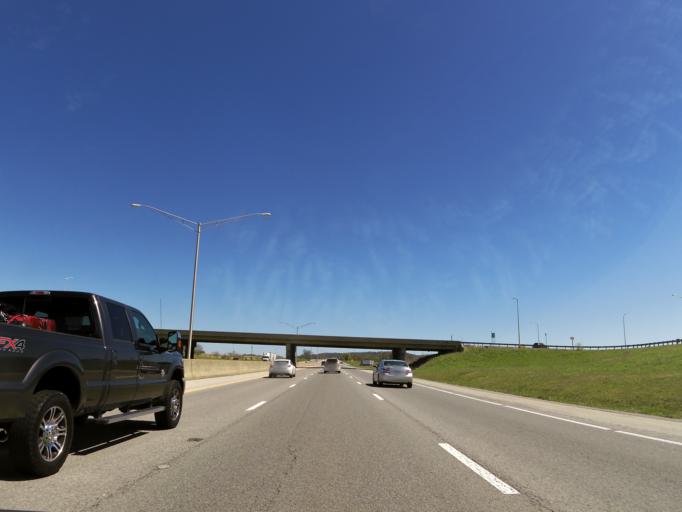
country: US
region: Kentucky
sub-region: Edmonson County
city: Brownsville
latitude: 37.0420
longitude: -86.2112
